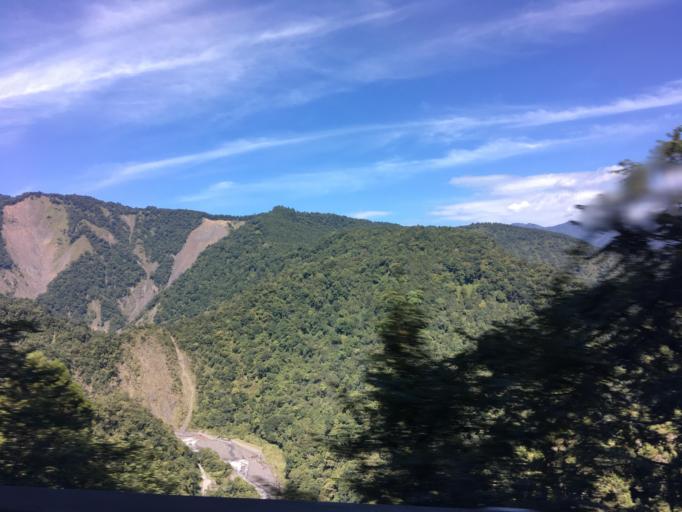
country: TW
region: Taiwan
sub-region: Yilan
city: Yilan
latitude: 24.5469
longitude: 121.5125
